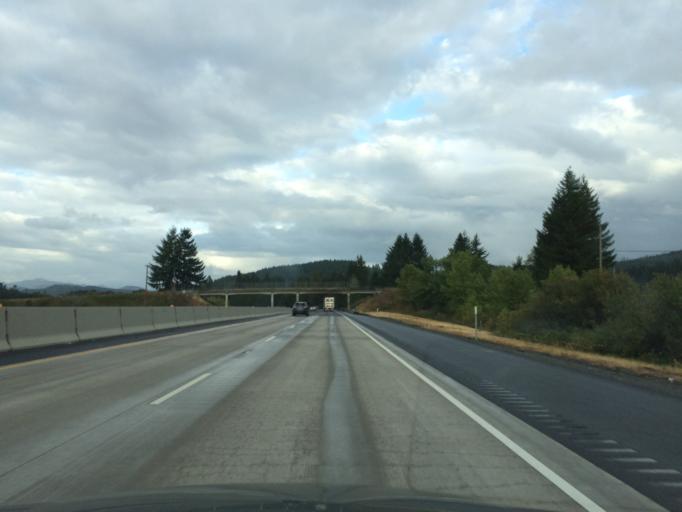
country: US
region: Oregon
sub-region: Lane County
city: Cottage Grove
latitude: 43.7501
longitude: -123.1163
